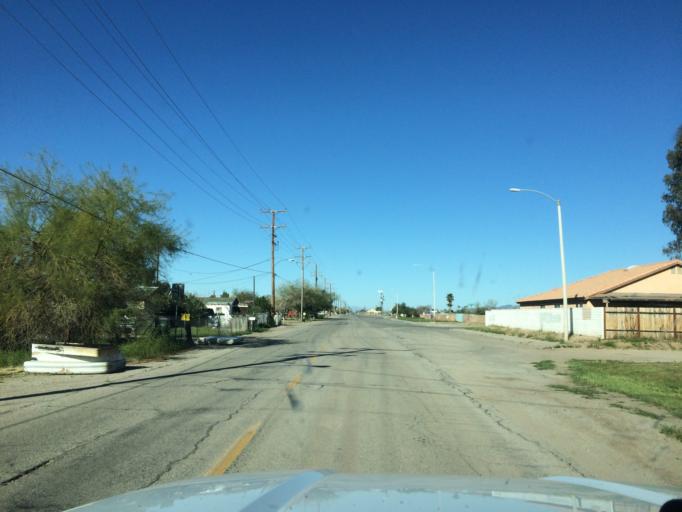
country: US
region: California
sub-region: Riverside County
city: Blythe
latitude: 33.6034
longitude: -114.5803
